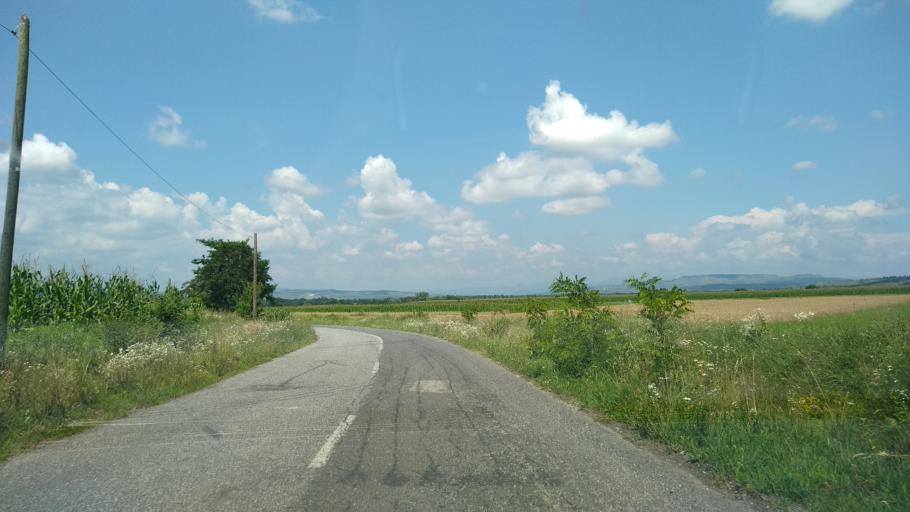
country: RO
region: Hunedoara
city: Berca
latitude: 45.6376
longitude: 23.0315
